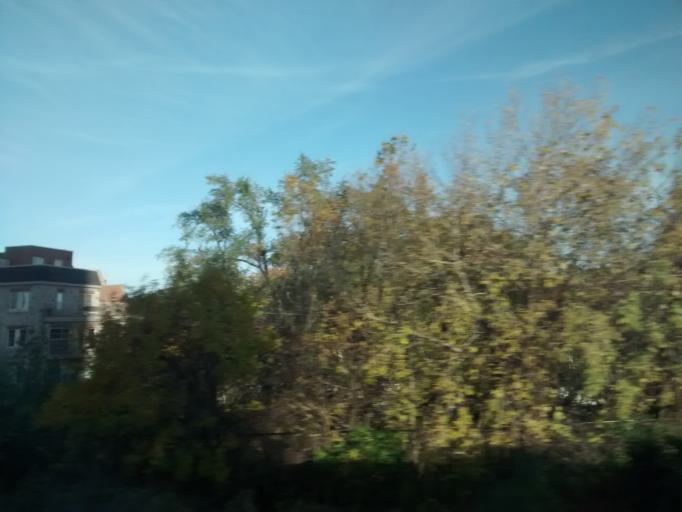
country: CA
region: Ontario
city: Toronto
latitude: 43.6371
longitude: -79.4667
